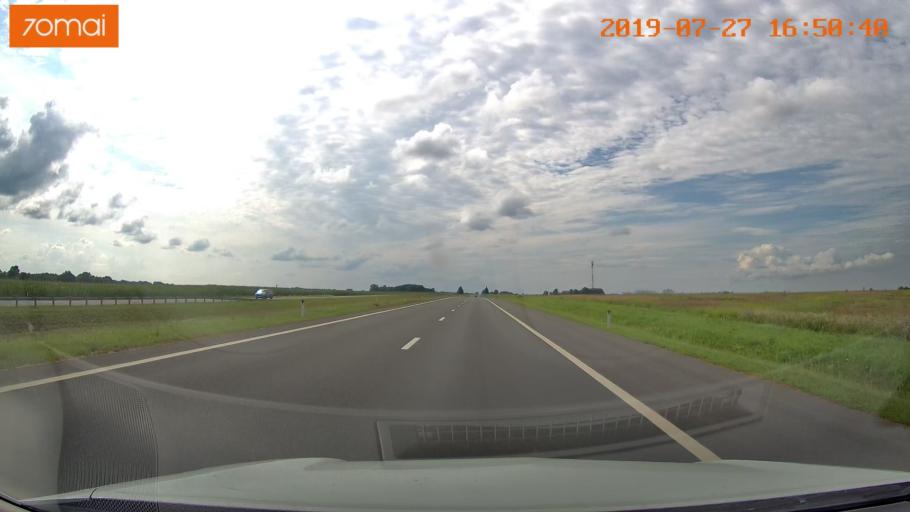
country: RU
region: Kaliningrad
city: Gvardeysk
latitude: 54.6787
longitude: 20.9076
